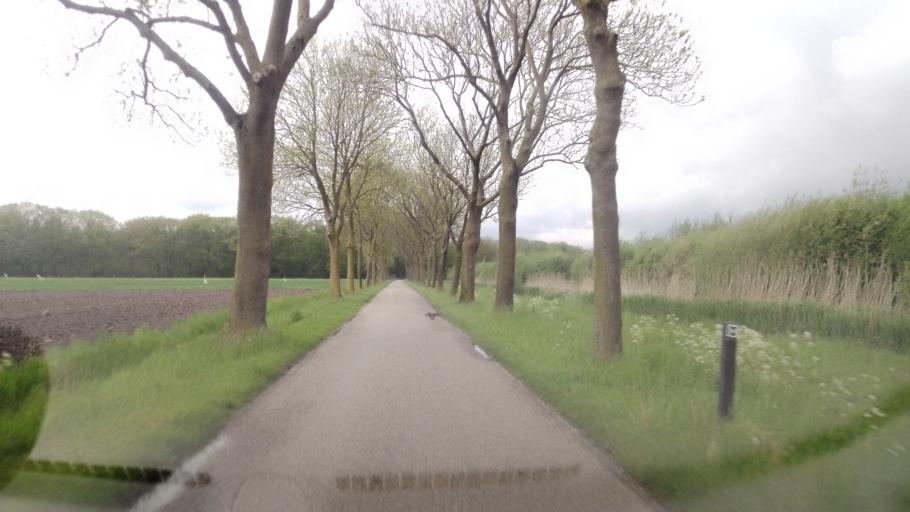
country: NL
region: Limburg
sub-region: Gemeente Venlo
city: Arcen
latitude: 51.4681
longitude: 6.2166
